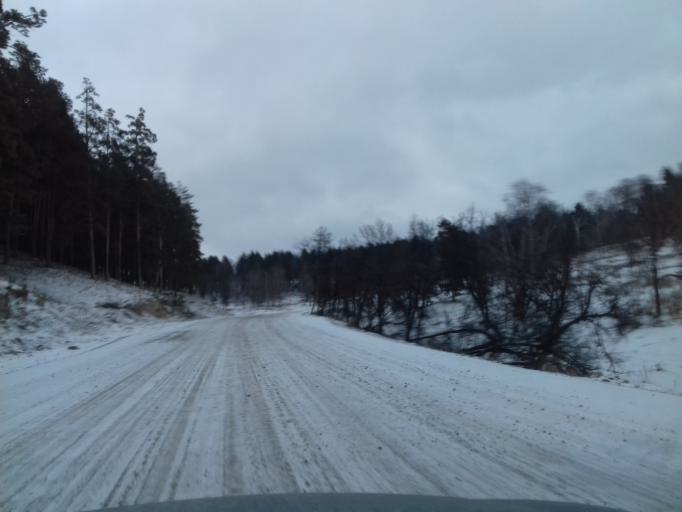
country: RU
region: Bashkortostan
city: Starosubkhangulovo
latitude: 53.0891
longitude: 57.4294
